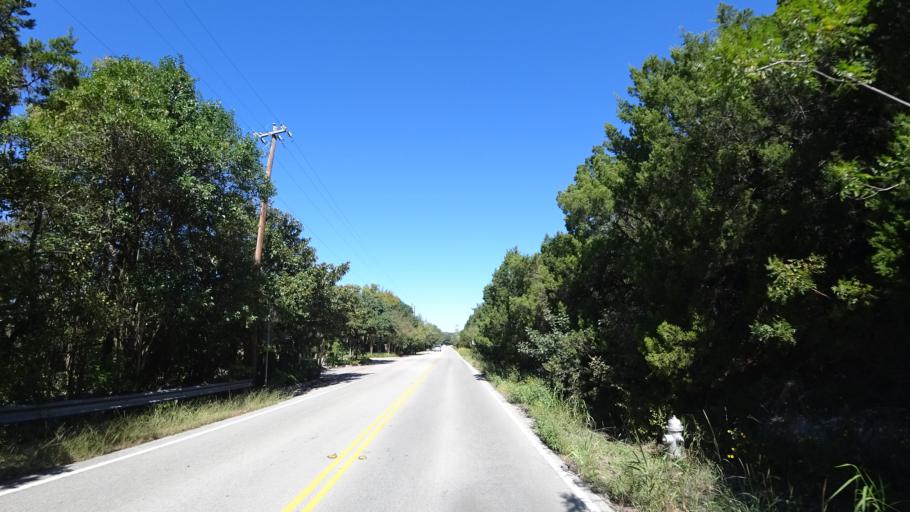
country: US
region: Texas
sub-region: Travis County
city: West Lake Hills
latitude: 30.3287
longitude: -97.7756
